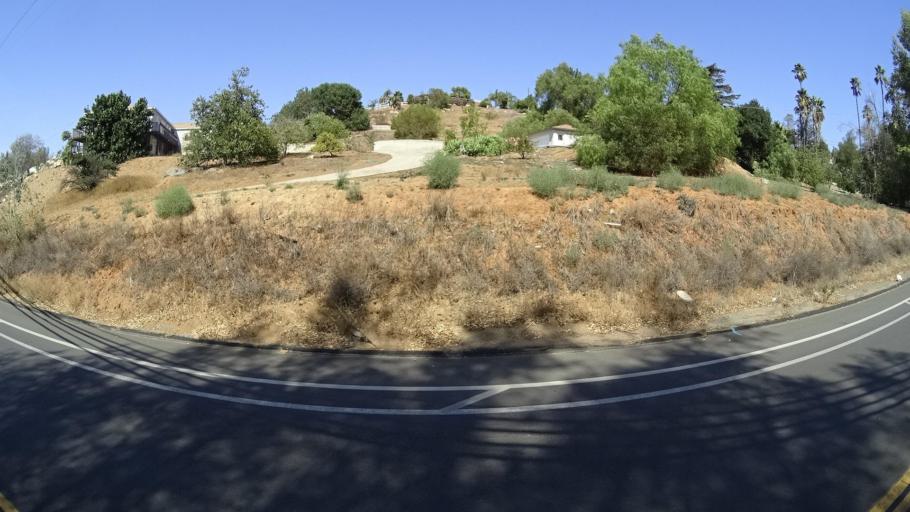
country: US
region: California
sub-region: San Diego County
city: Granite Hills
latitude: 32.7861
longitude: -116.9135
